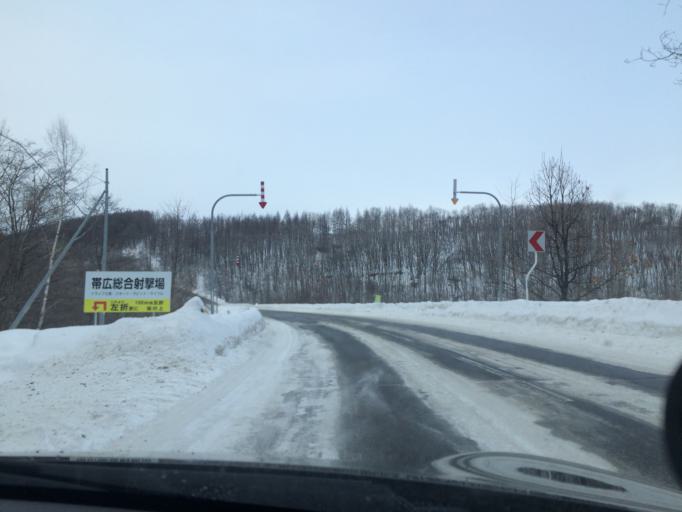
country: JP
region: Hokkaido
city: Otofuke
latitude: 43.0025
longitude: 143.0372
